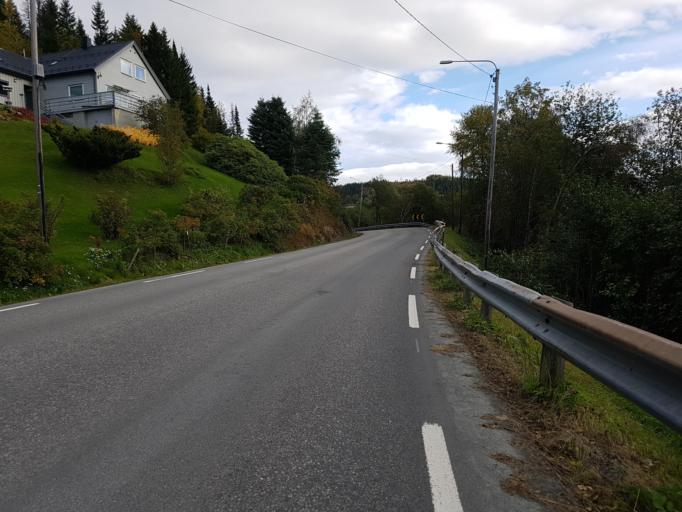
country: NO
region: Sor-Trondelag
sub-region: Klaebu
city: Klaebu
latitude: 63.3974
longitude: 10.5364
